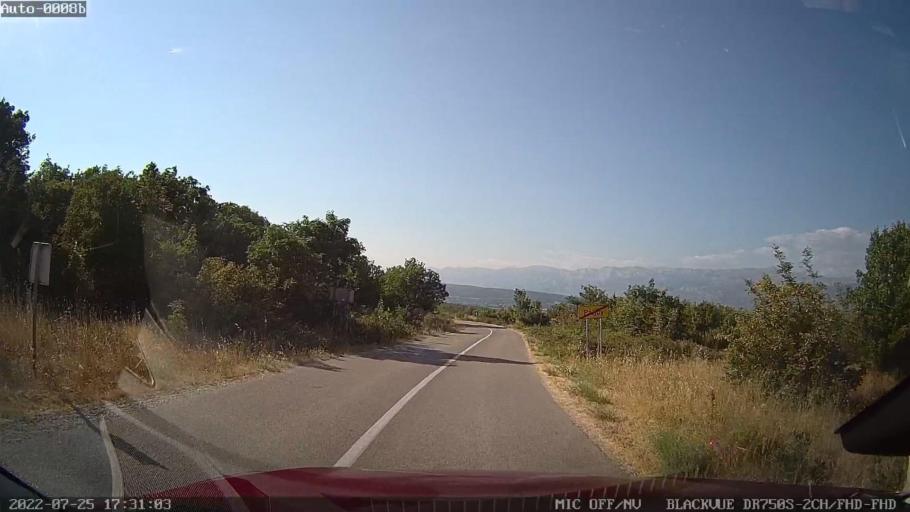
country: HR
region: Zadarska
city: Posedarje
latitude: 44.1683
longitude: 15.5026
